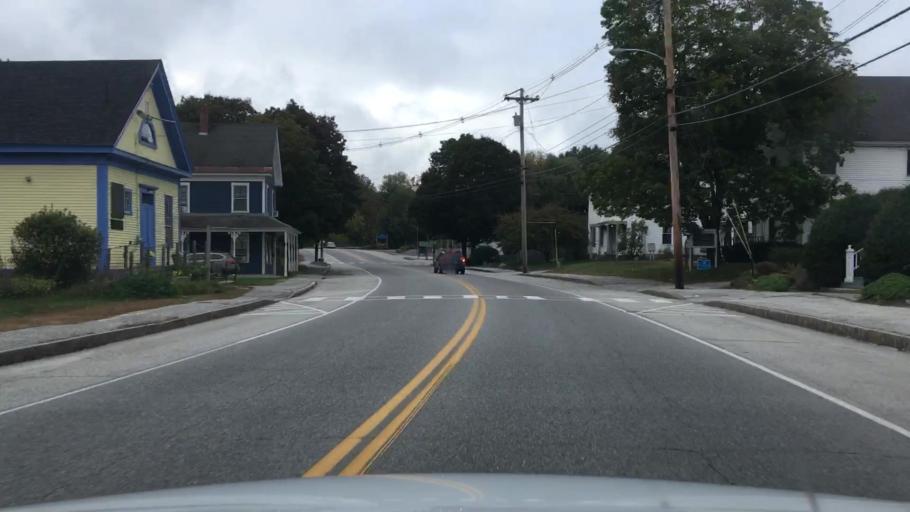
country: US
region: Maine
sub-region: Oxford County
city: Norway
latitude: 44.2141
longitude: -70.5444
